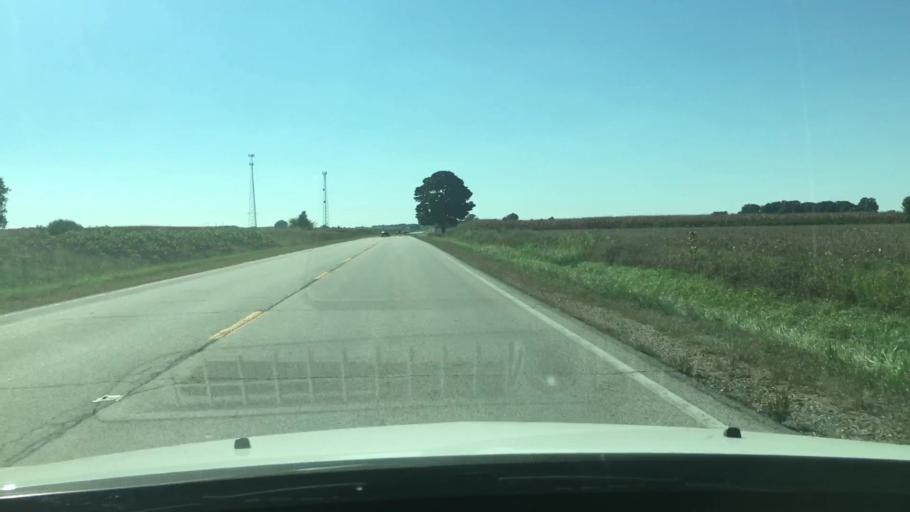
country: US
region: Illinois
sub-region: DeKalb County
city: Waterman
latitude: 41.7690
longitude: -88.8107
